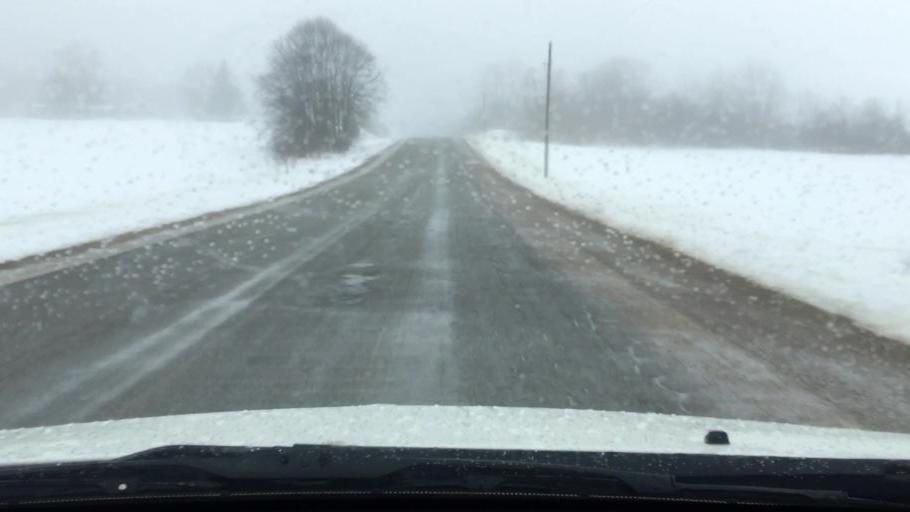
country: US
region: Michigan
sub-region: Charlevoix County
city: East Jordan
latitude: 45.1326
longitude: -85.1629
